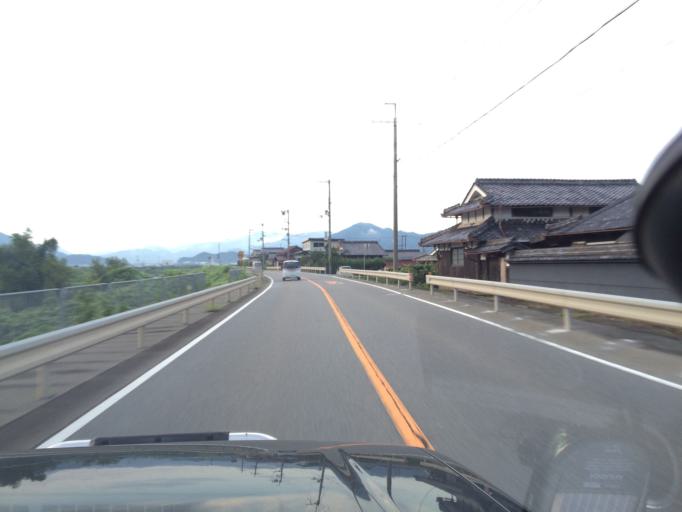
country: JP
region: Hyogo
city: Nishiwaki
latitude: 35.1397
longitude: 135.0278
